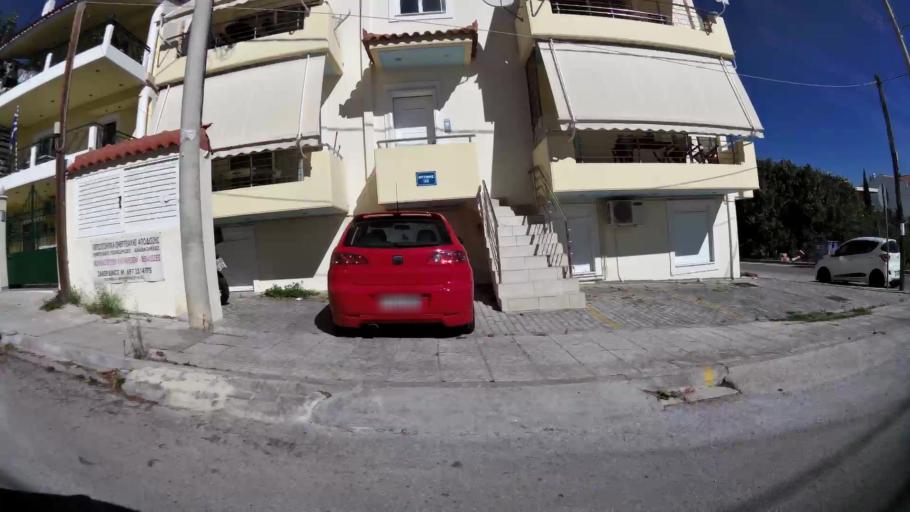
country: GR
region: Attica
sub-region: Nomarchia Anatolikis Attikis
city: Leondarion
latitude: 38.0009
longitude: 23.8520
